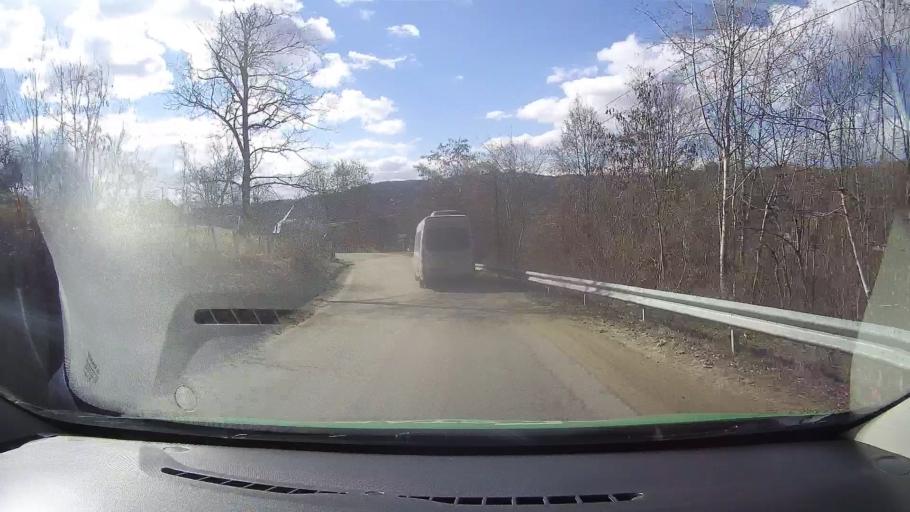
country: RO
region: Dambovita
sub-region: Comuna Runcu
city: Badeni
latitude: 45.1462
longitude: 25.4032
